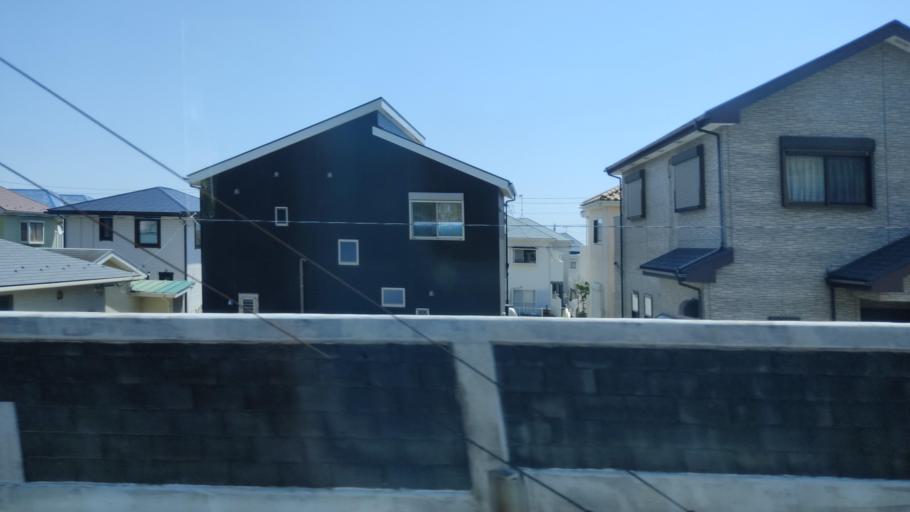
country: JP
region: Kanagawa
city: Oiso
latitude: 35.3140
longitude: 139.3174
